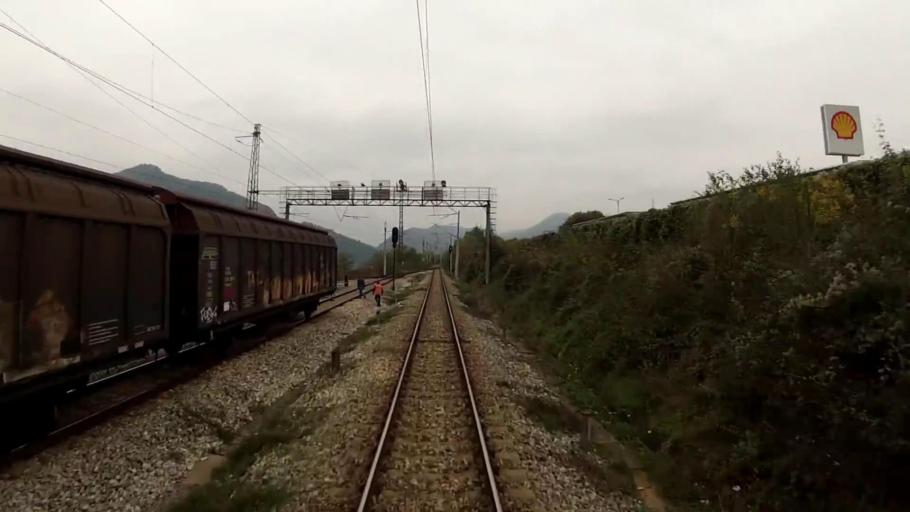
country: RS
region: Central Serbia
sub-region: Pirotski Okrug
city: Dimitrovgrad
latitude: 42.9899
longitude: 22.8516
